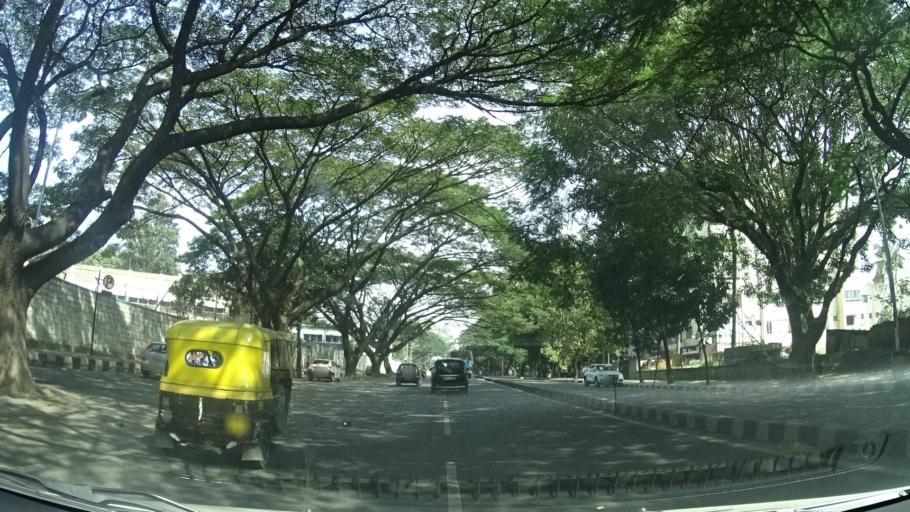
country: IN
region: Karnataka
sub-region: Bangalore Urban
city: Bangalore
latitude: 13.0150
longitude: 77.5776
